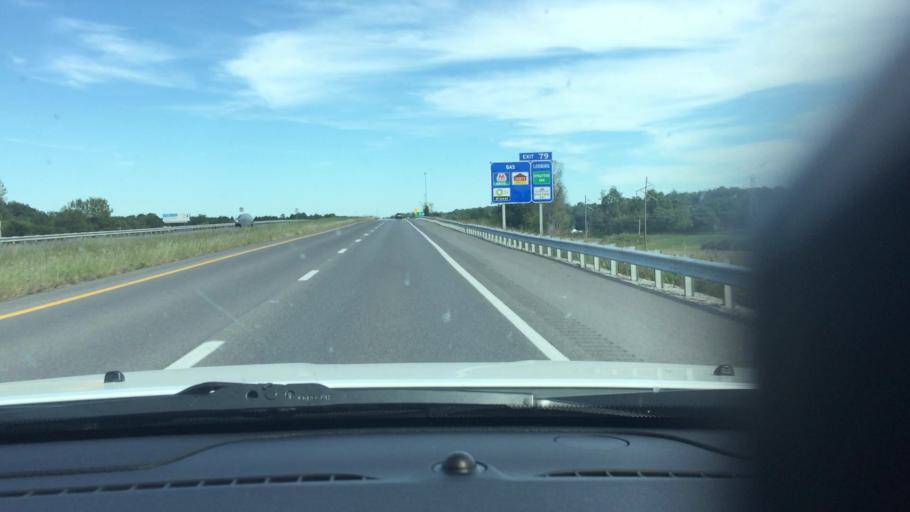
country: US
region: Kentucky
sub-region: Caldwell County
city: Princeton
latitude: 37.1204
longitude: -87.9033
